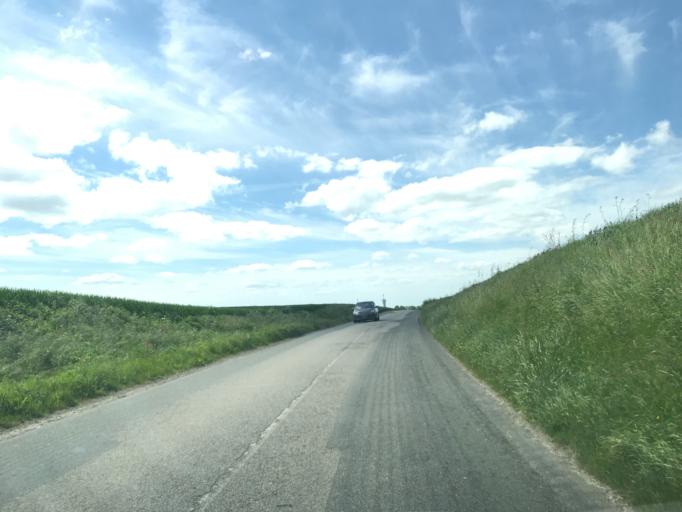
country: FR
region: Haute-Normandie
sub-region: Departement de l'Eure
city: Le Neubourg
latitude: 49.1483
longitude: 0.8787
